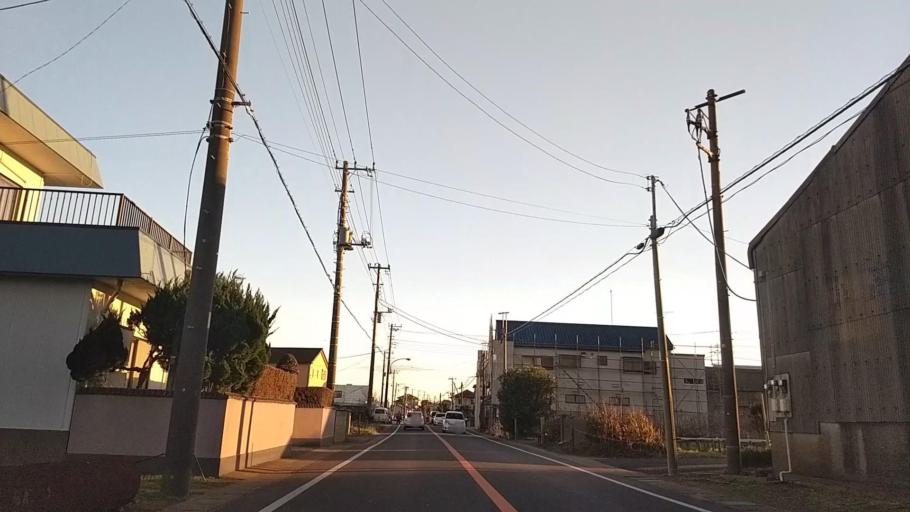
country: JP
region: Chiba
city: Hasaki
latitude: 35.7353
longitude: 140.8630
